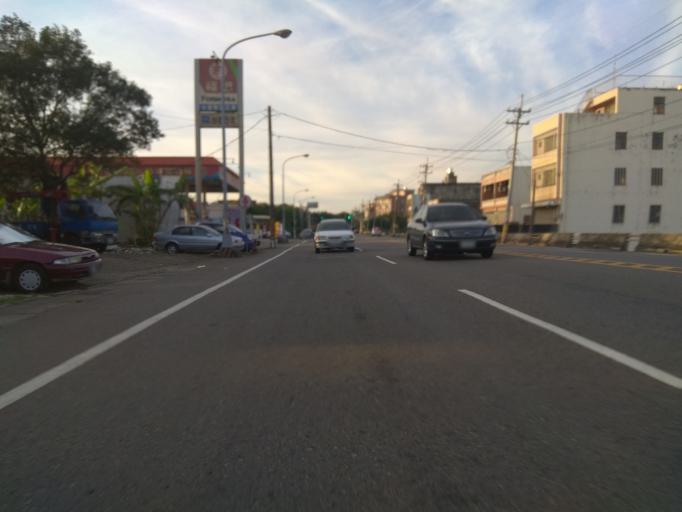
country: TW
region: Taiwan
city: Taoyuan City
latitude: 24.9751
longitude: 121.1970
